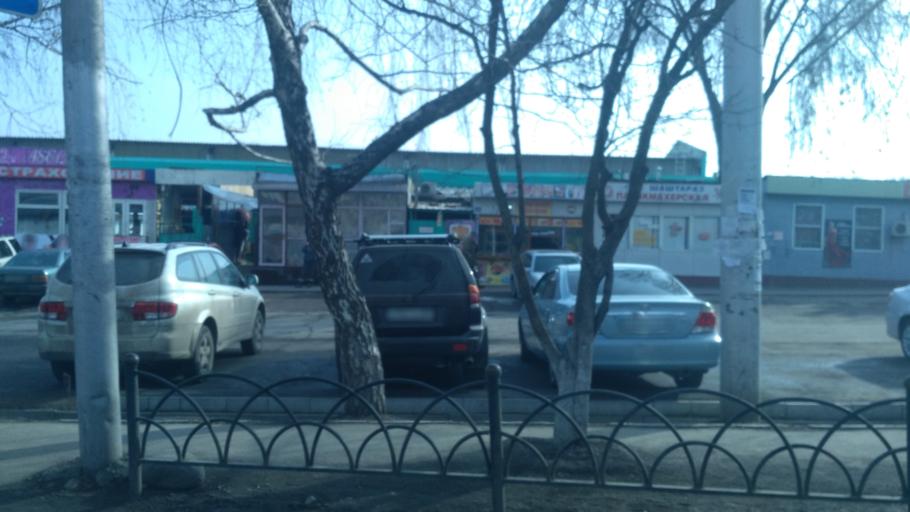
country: KZ
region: Almaty Qalasy
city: Almaty
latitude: 43.2306
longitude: 76.8334
